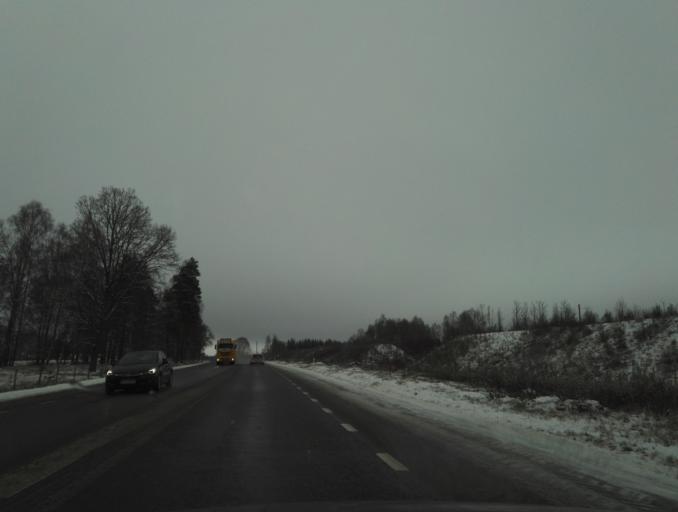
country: SE
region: Kronoberg
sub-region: Vaxjo Kommun
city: Vaexjoe
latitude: 56.8702
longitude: 14.7400
